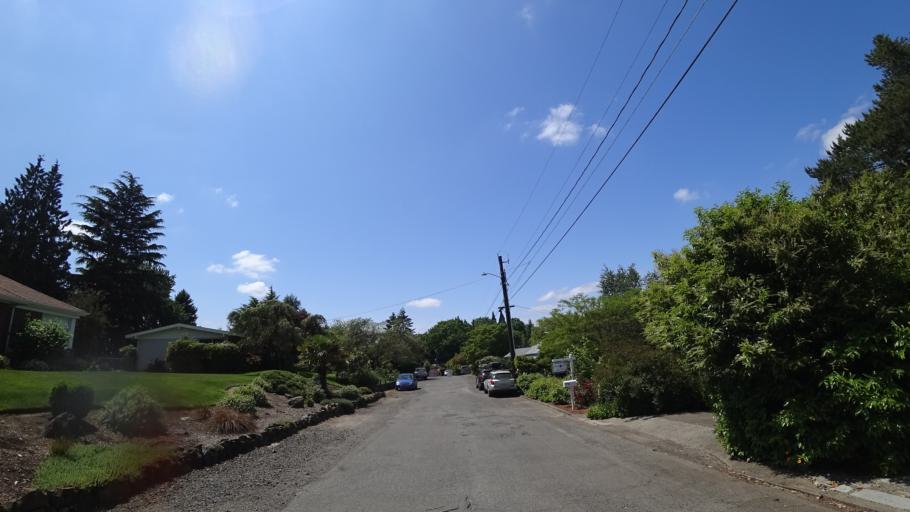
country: US
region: Oregon
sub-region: Clackamas County
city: Lake Oswego
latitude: 45.4697
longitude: -122.6978
